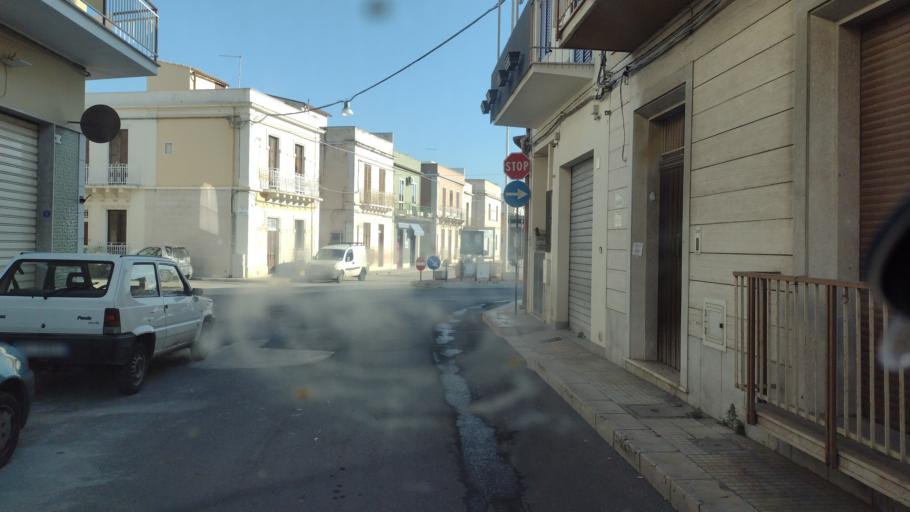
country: IT
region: Sicily
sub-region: Provincia di Siracusa
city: Avola
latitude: 36.9103
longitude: 15.1392
